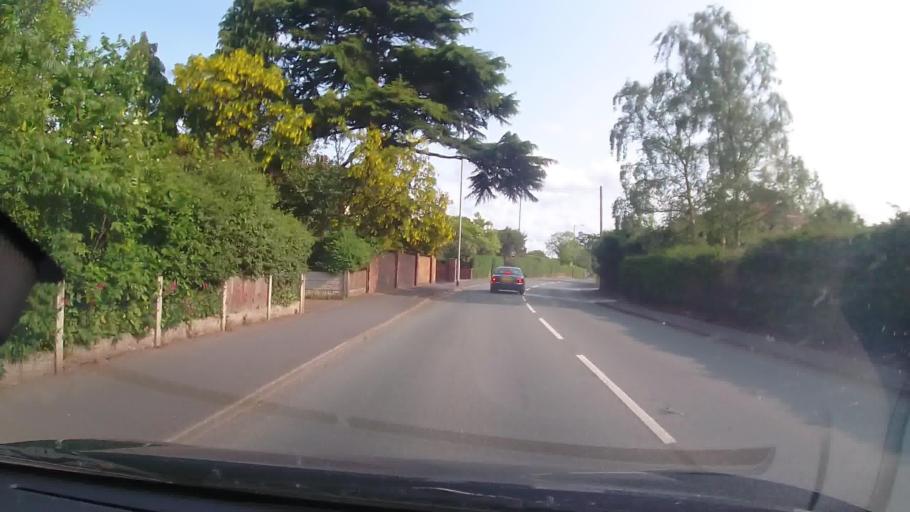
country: GB
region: England
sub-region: Shropshire
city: Shrewsbury
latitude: 52.7244
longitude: -2.7521
